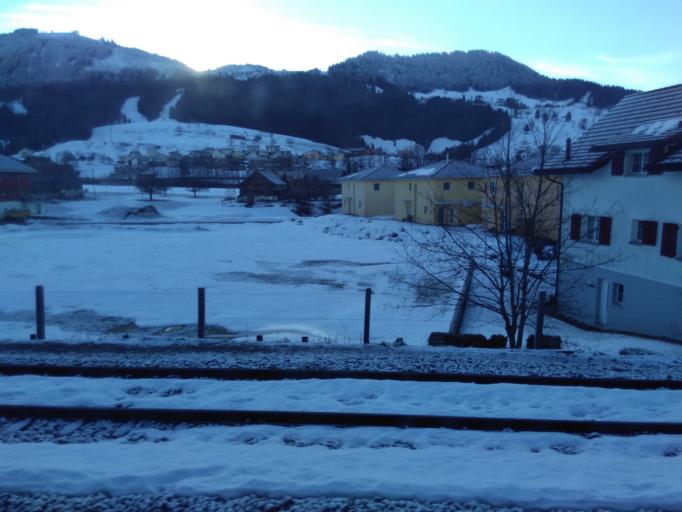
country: CH
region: Schwyz
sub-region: Bezirk Schwyz
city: Sattel
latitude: 47.0791
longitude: 8.6257
